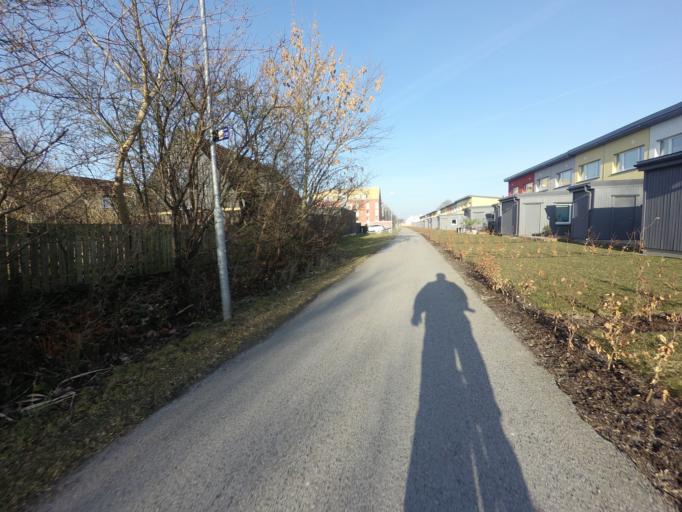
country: SE
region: Skane
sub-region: Hoganas Kommun
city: Hoganas
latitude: 56.2011
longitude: 12.5752
